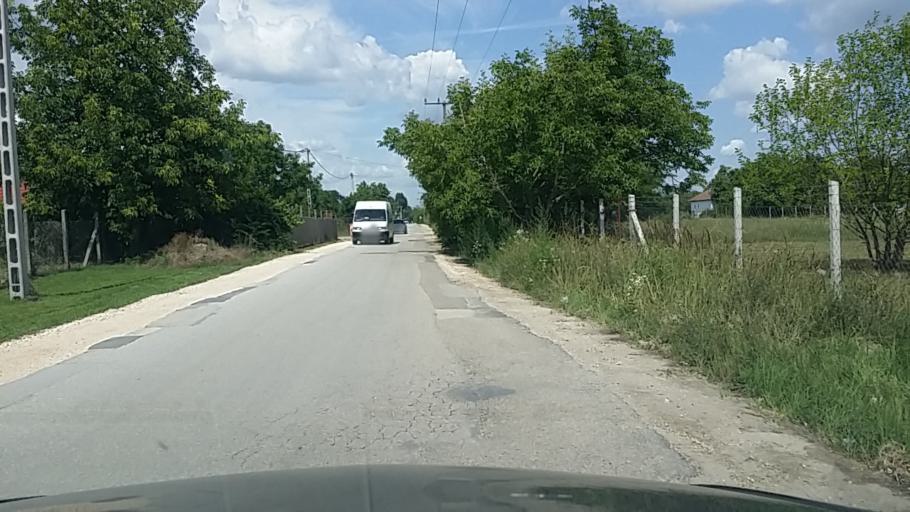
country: HU
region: Bacs-Kiskun
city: Kecskemet
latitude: 46.9224
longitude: 19.6560
